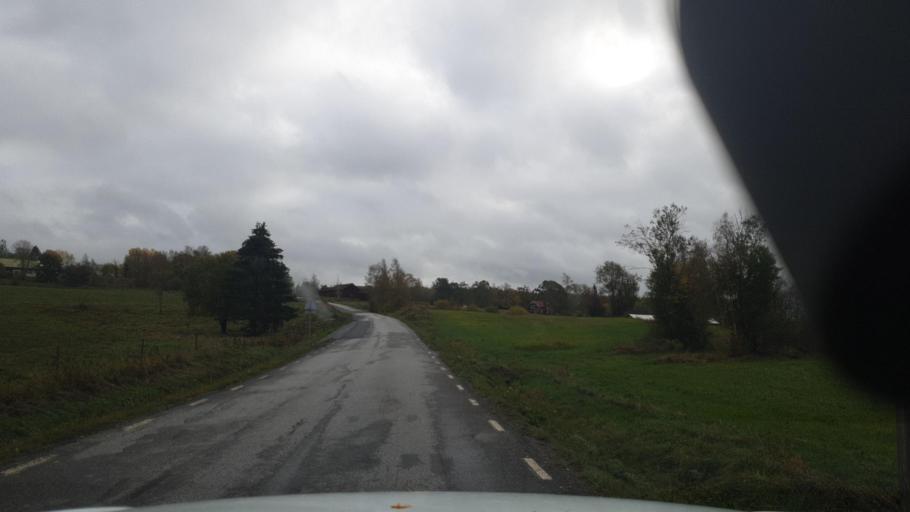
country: SE
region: Vaermland
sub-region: Karlstads Kommun
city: Valberg
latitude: 59.4213
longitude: 13.1035
